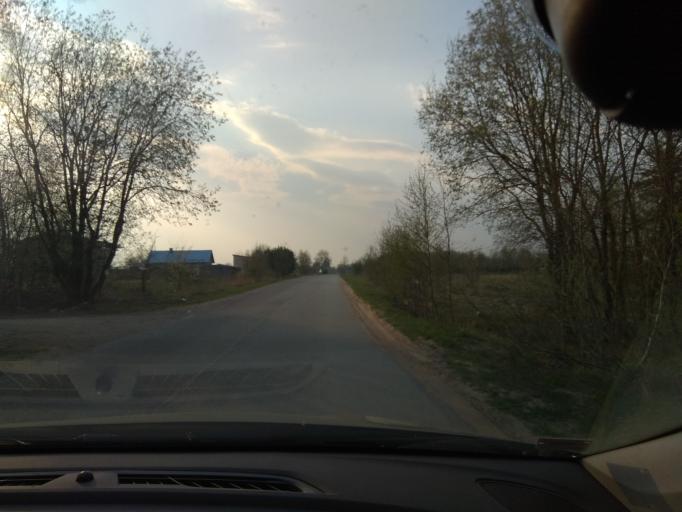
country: LT
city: Baltoji Voke
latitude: 54.5937
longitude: 25.1544
